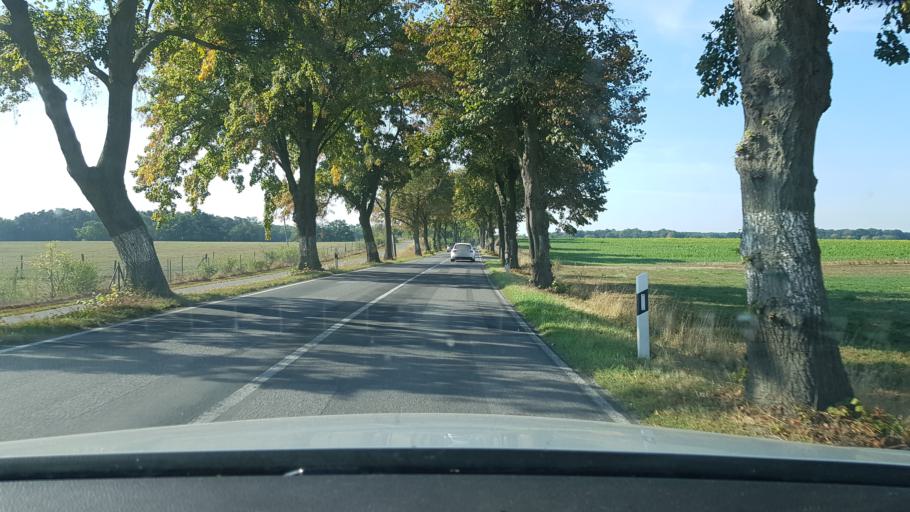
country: DE
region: Brandenburg
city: Mixdorf
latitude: 52.1635
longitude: 14.3283
